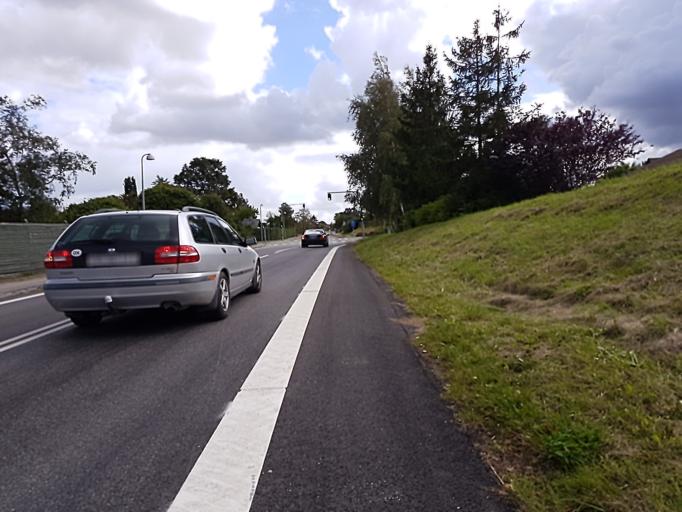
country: DK
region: Zealand
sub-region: Roskilde Kommune
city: Gundsomagle
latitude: 55.7399
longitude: 12.1478
